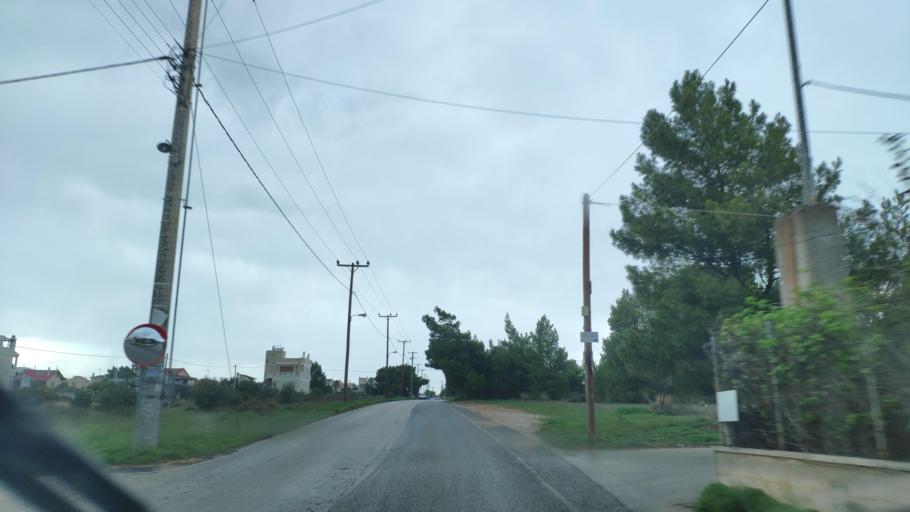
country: GR
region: Attica
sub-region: Nomarchia Anatolikis Attikis
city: Rafina
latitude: 37.9934
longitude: 24.0192
